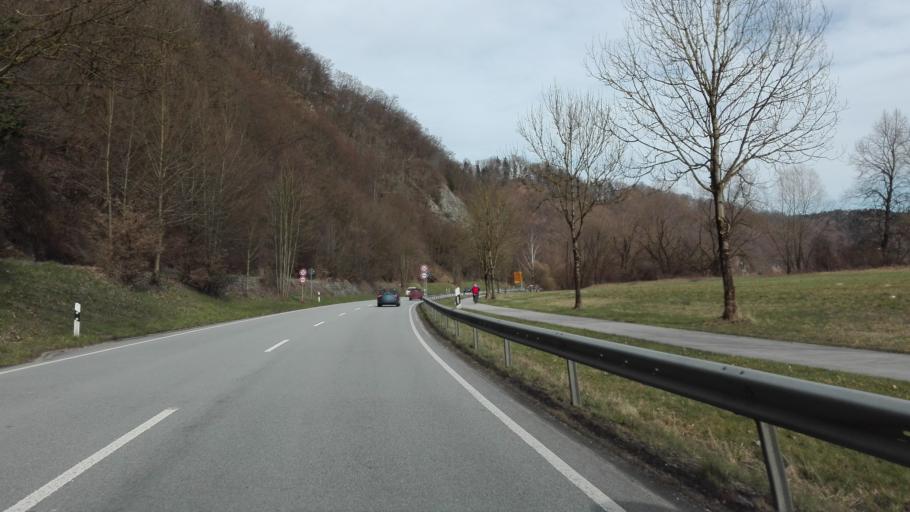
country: DE
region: Bavaria
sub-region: Lower Bavaria
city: Witzmannsberg
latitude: 48.5912
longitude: 13.5067
